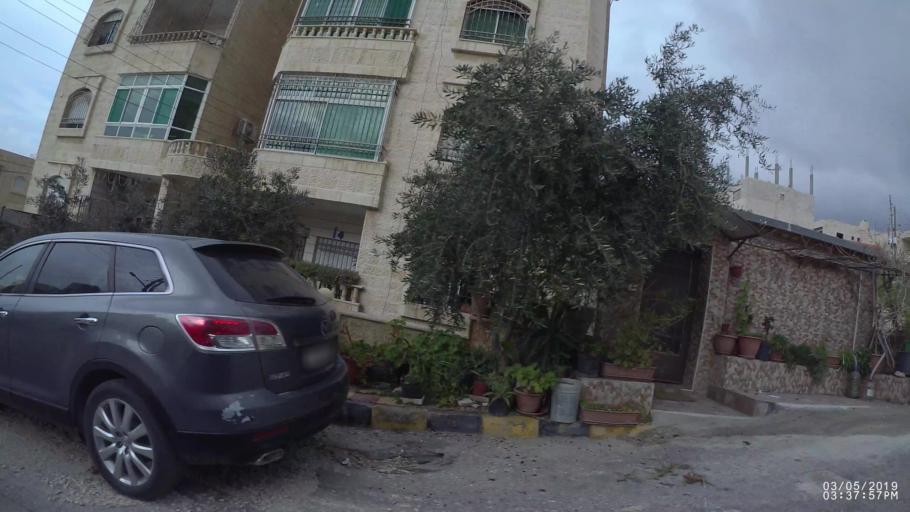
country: JO
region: Amman
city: Amman
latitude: 32.0054
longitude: 35.9424
